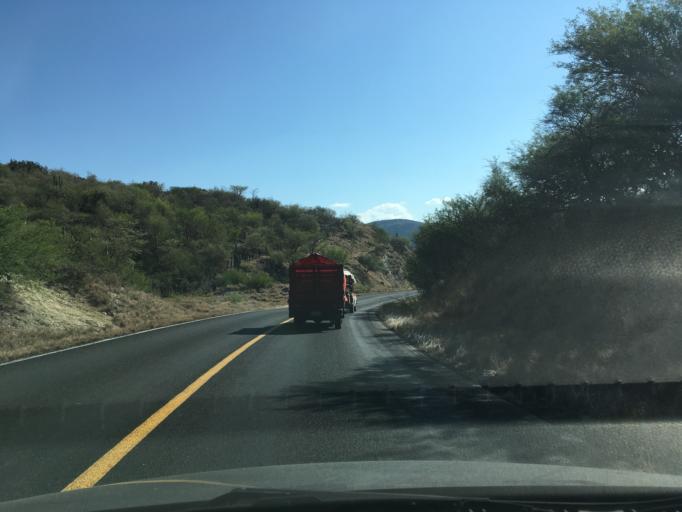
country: MX
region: Hidalgo
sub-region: San Agustin Metzquititlan
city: Mezquititlan
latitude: 20.4609
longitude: -98.6790
